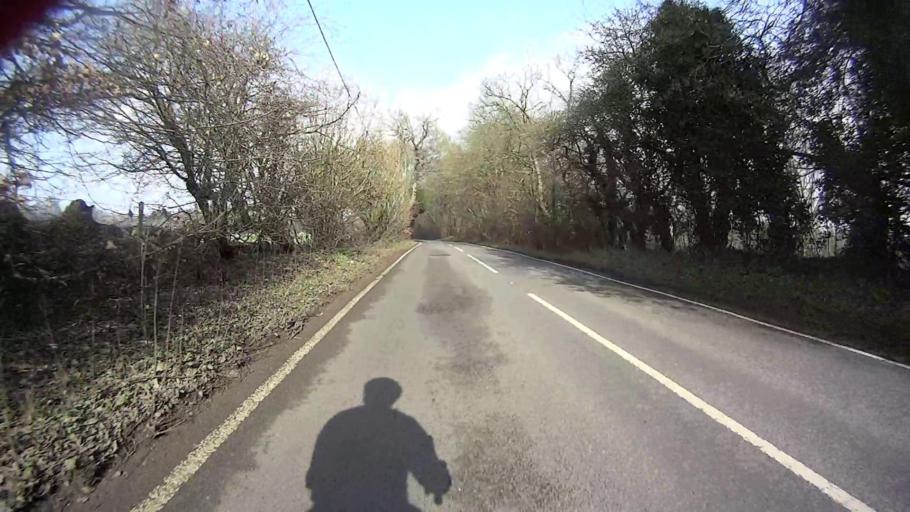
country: GB
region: England
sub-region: Surrey
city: Headley
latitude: 51.2589
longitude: -0.2699
